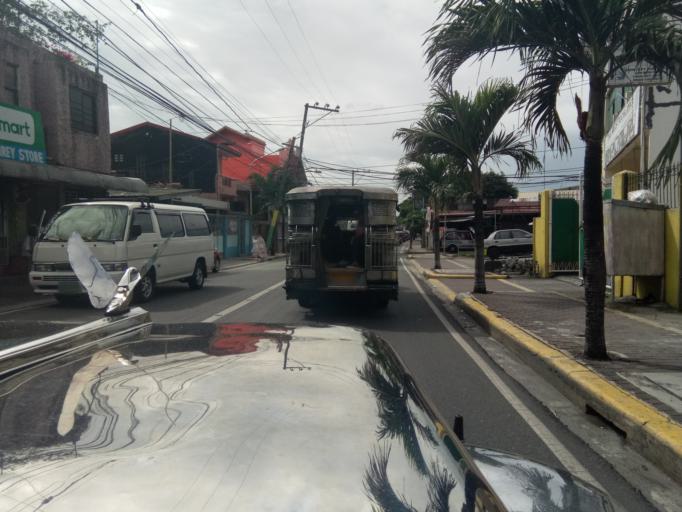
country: PH
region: Calabarzon
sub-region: Province of Cavite
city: Dasmarinas
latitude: 14.3180
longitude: 120.9422
